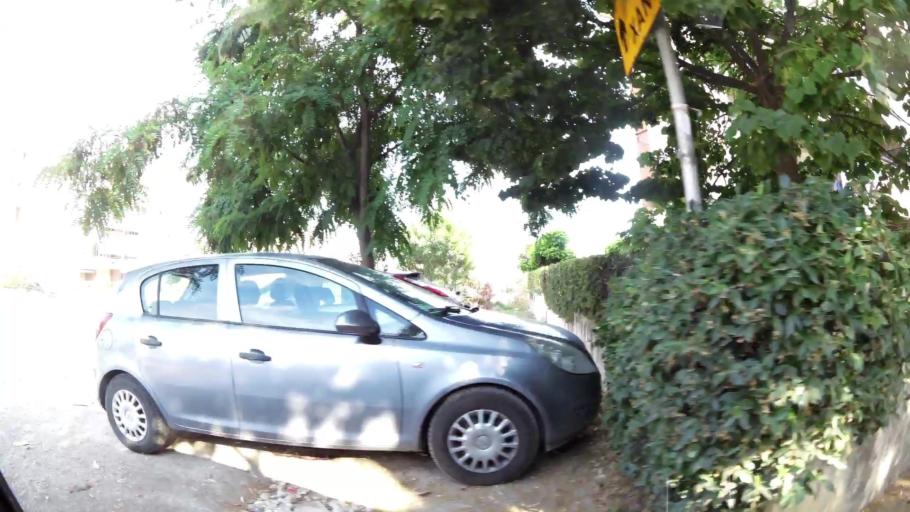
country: GR
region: Central Macedonia
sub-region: Nomos Thessalonikis
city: Kalamaria
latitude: 40.5702
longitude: 22.9634
